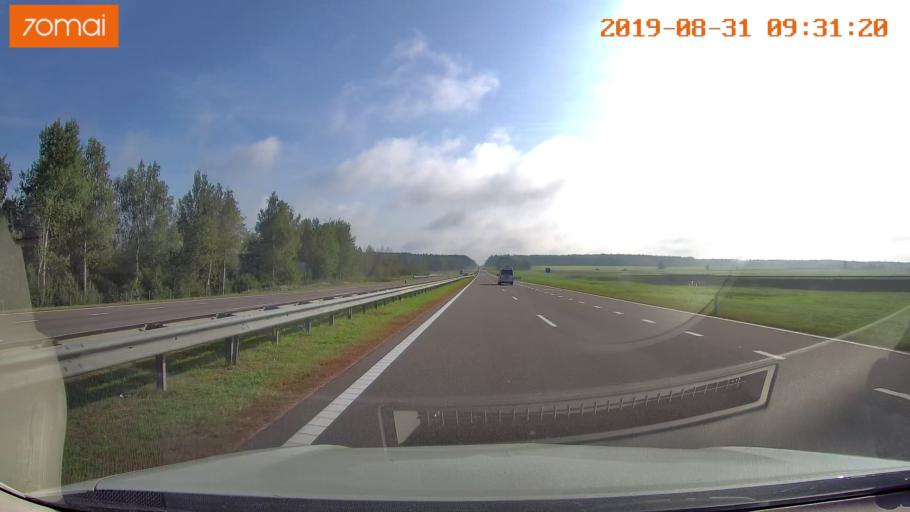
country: BY
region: Minsk
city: Byerazino
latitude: 53.8568
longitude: 29.1487
